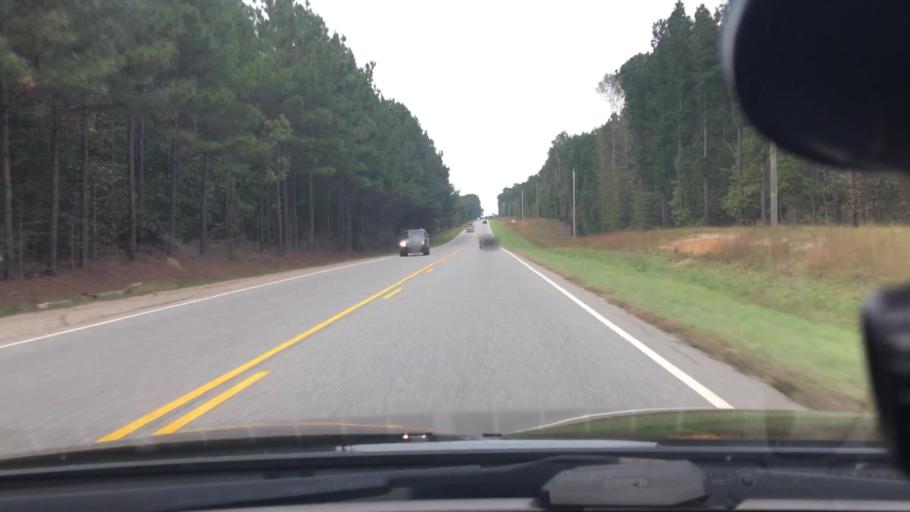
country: US
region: North Carolina
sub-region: Montgomery County
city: Biscoe
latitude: 35.3664
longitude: -79.6799
